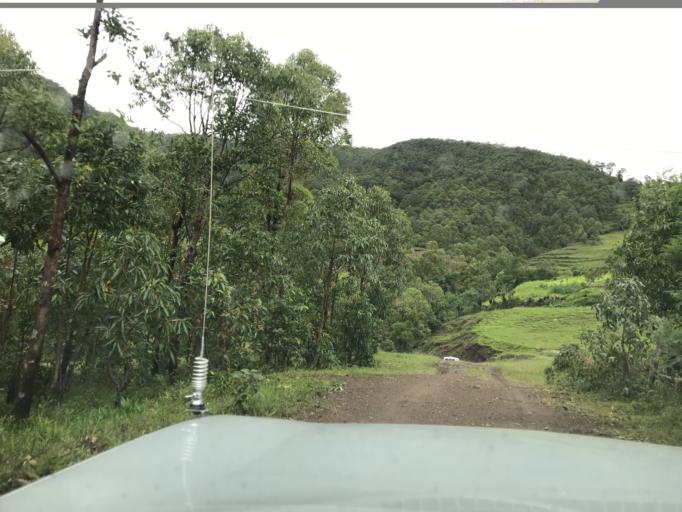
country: TL
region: Ainaro
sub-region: Ainaro
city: Ainaro
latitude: -8.8675
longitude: 125.5528
